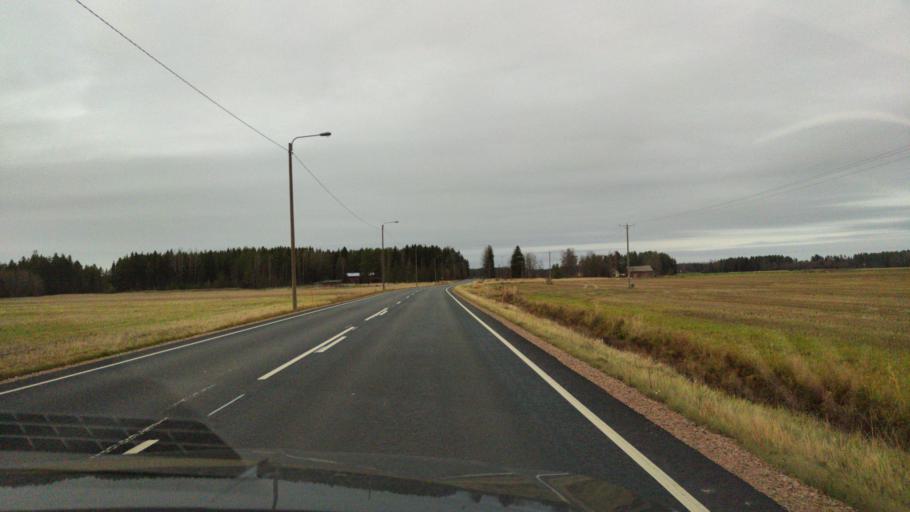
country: FI
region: Varsinais-Suomi
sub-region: Turku
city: Vahto
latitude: 60.6650
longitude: 22.4346
